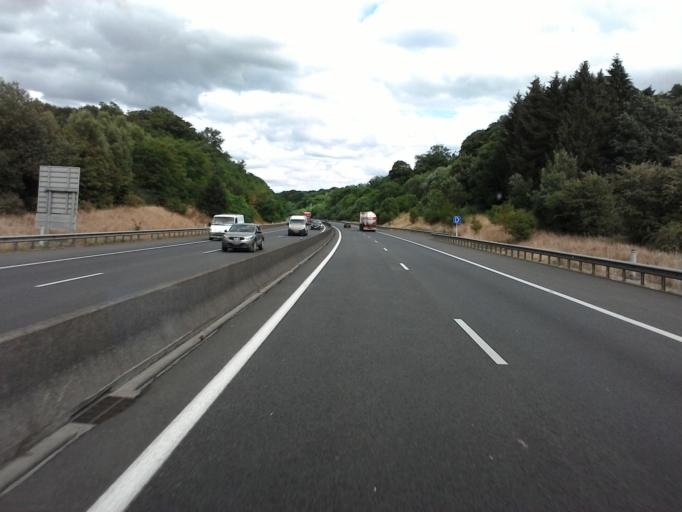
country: LU
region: Luxembourg
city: Capellen
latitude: 49.6346
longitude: 5.9806
